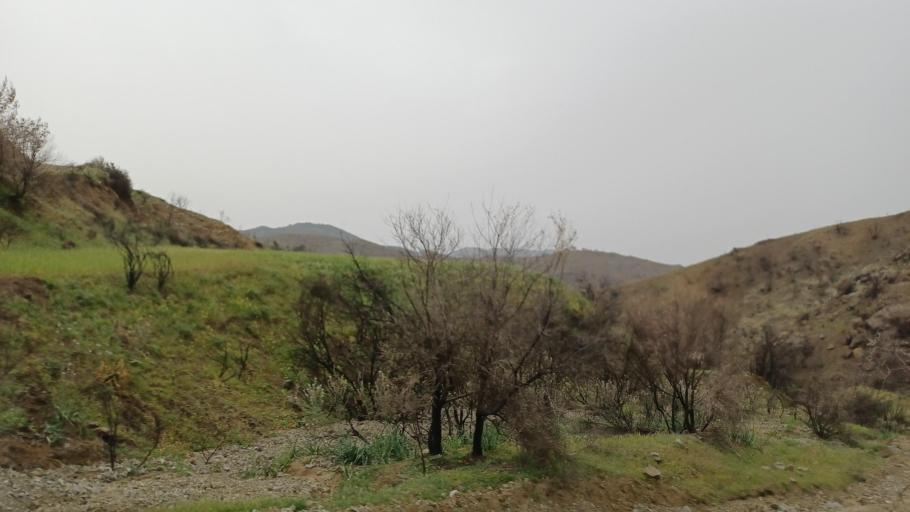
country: CY
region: Limassol
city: Parekklisha
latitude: 34.8517
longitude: 33.1392
